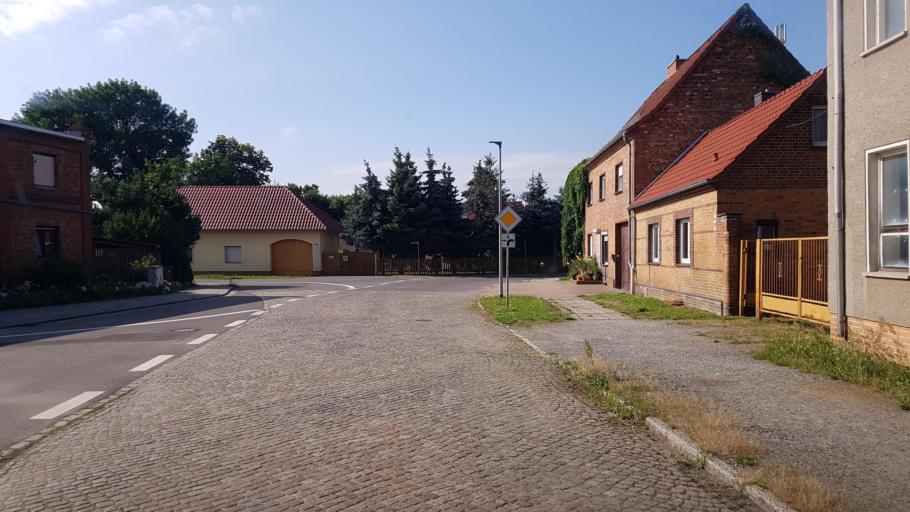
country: DE
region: Brandenburg
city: Grossraschen
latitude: 51.5498
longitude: 14.0580
